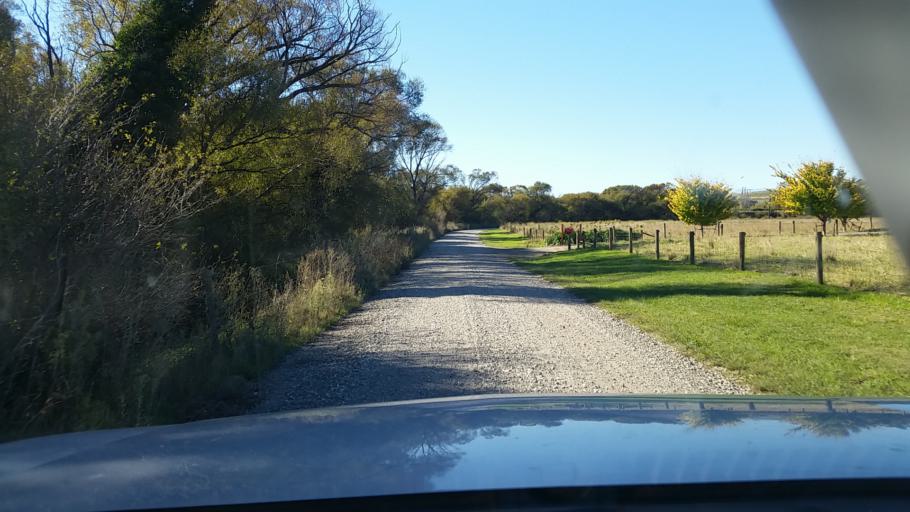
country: NZ
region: Marlborough
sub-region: Marlborough District
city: Blenheim
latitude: -41.6795
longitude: 174.1352
